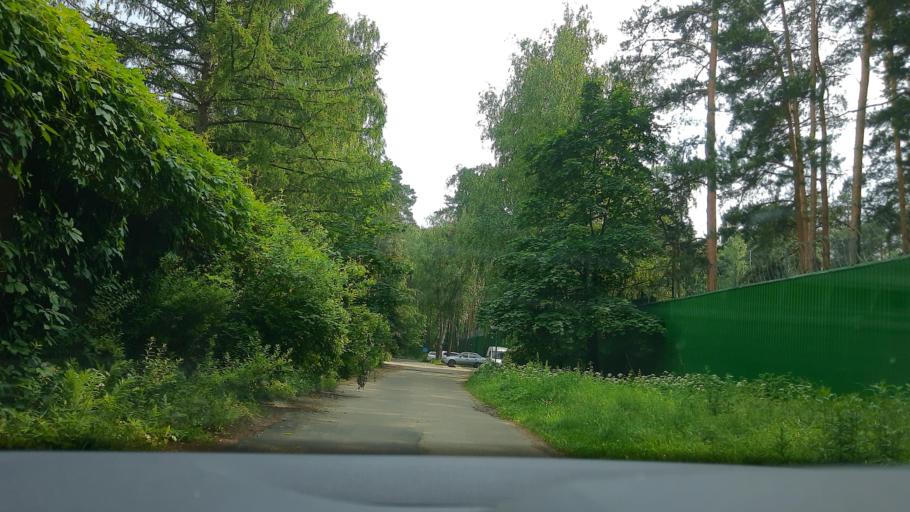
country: RU
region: Moscow
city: Rublevo
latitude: 55.7803
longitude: 37.3885
